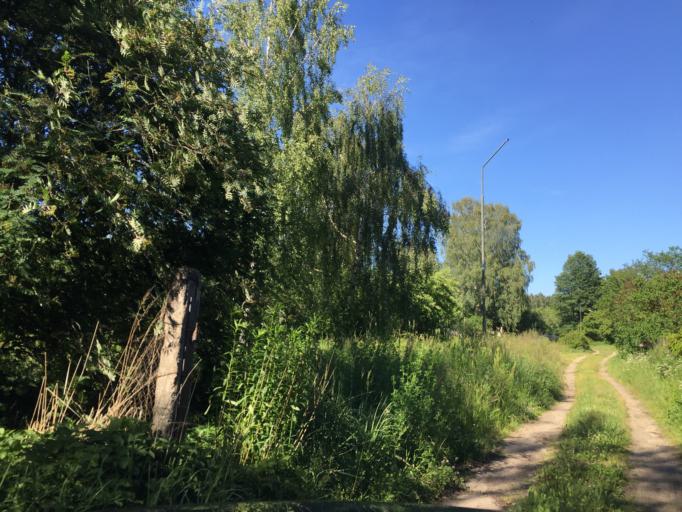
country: LV
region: Babite
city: Pinki
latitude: 56.9545
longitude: 23.9515
